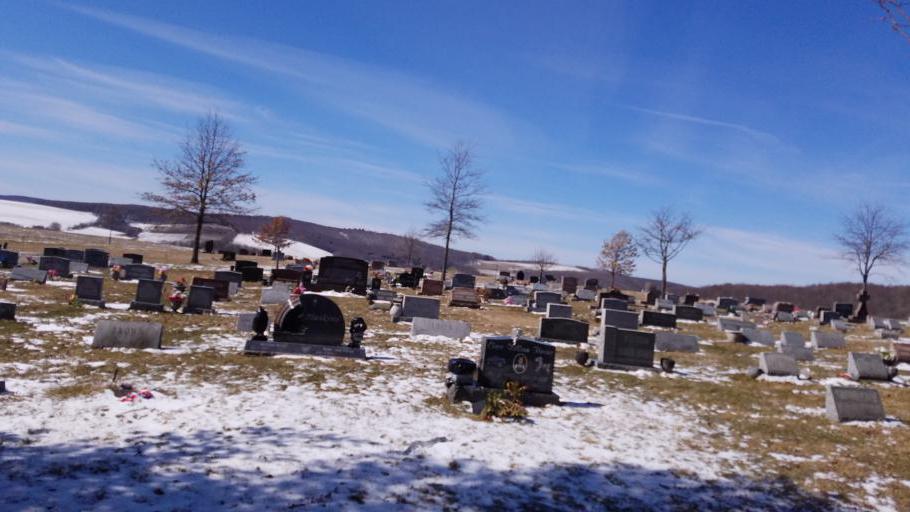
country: US
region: Pennsylvania
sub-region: Potter County
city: Galeton
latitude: 41.9101
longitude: -77.7592
